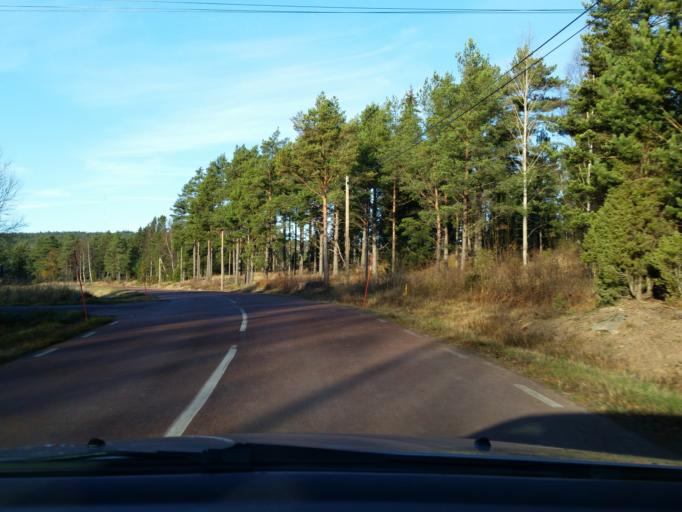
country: AX
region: Alands landsbygd
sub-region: Sund
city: Sund
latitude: 60.3083
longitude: 20.1787
